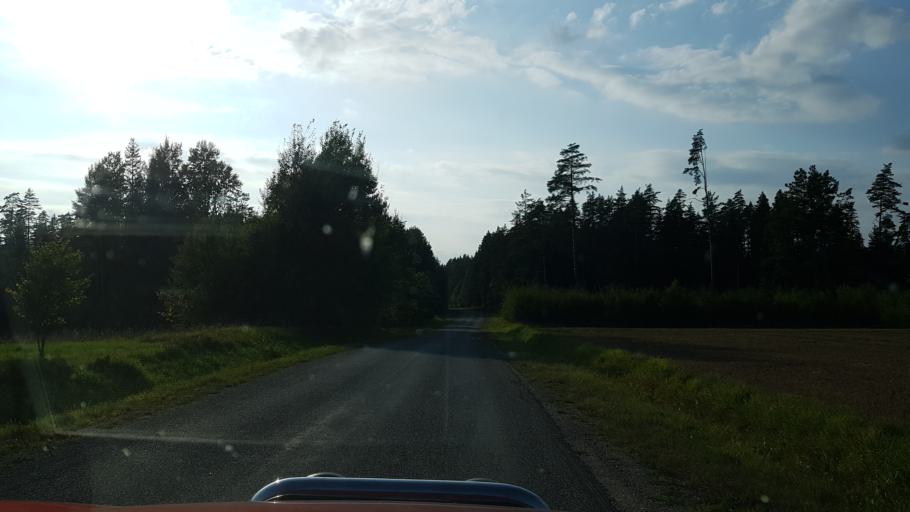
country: EE
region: Polvamaa
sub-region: Polva linn
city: Polva
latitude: 58.1252
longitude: 26.9469
